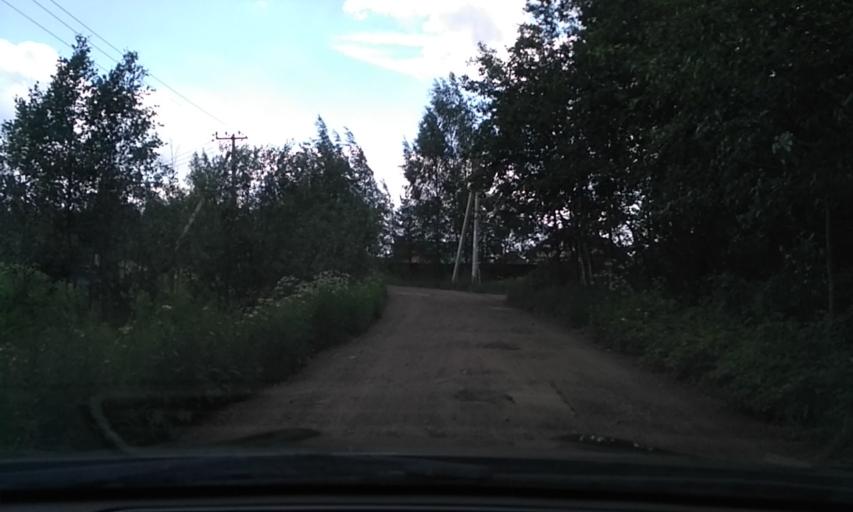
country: RU
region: Leningrad
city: Otradnoye
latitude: 59.8155
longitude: 30.8257
